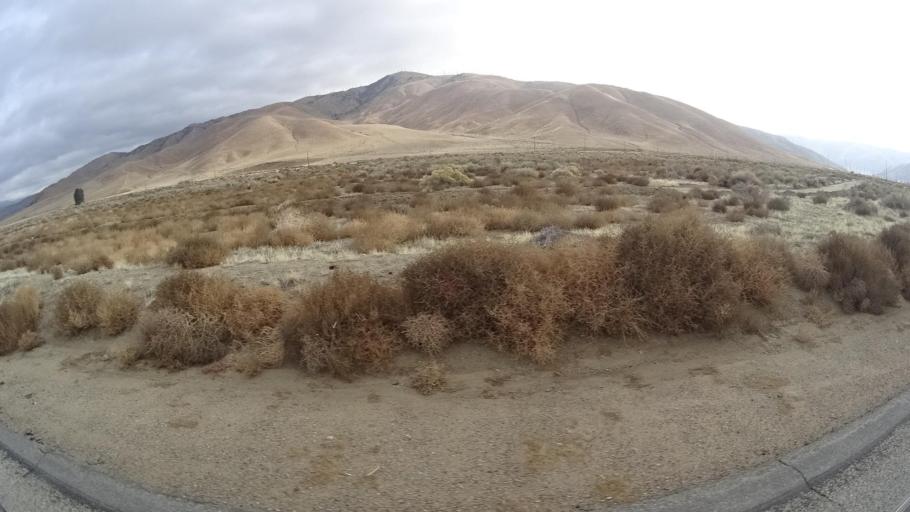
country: US
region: California
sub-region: Kern County
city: Tehachapi
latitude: 35.1188
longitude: -118.3253
